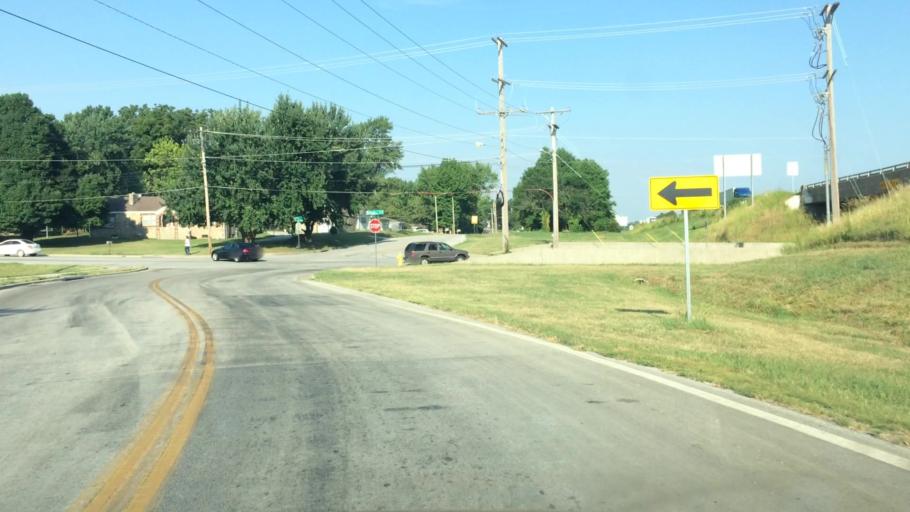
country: US
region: Missouri
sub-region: Greene County
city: Springfield
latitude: 37.2500
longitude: -93.2737
